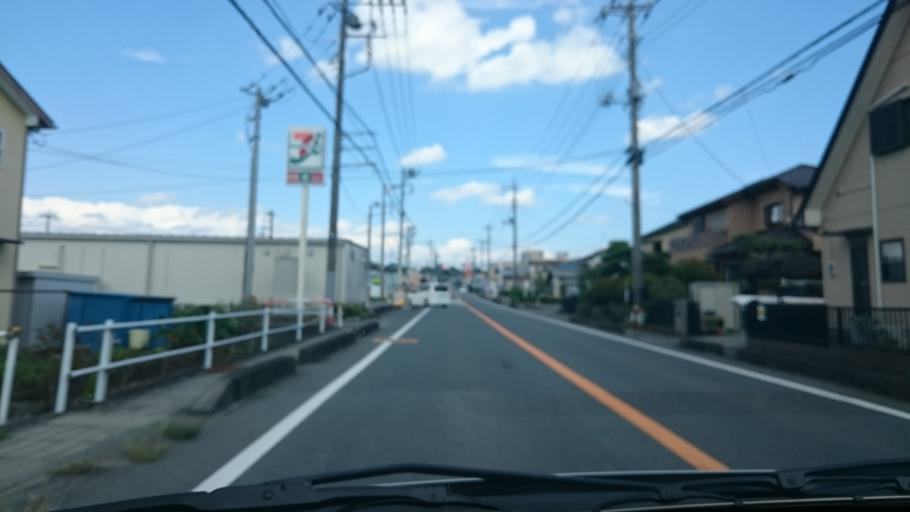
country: JP
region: Shizuoka
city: Gotemba
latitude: 35.2263
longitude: 138.9199
